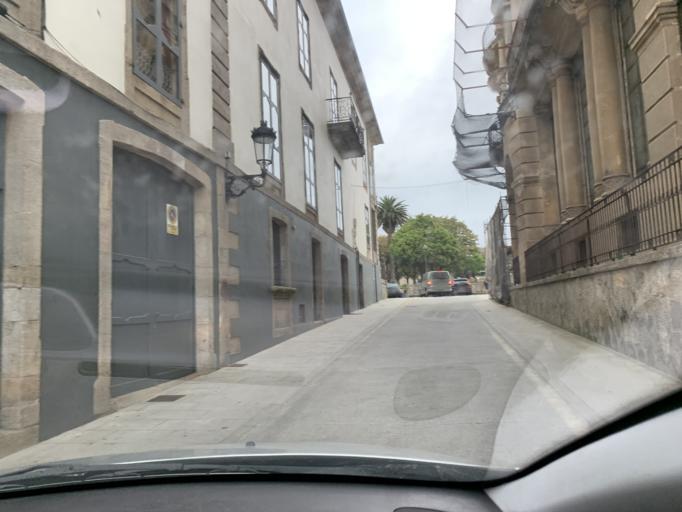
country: ES
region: Galicia
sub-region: Provincia de Lugo
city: Ribadeo
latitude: 43.5365
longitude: -7.0394
